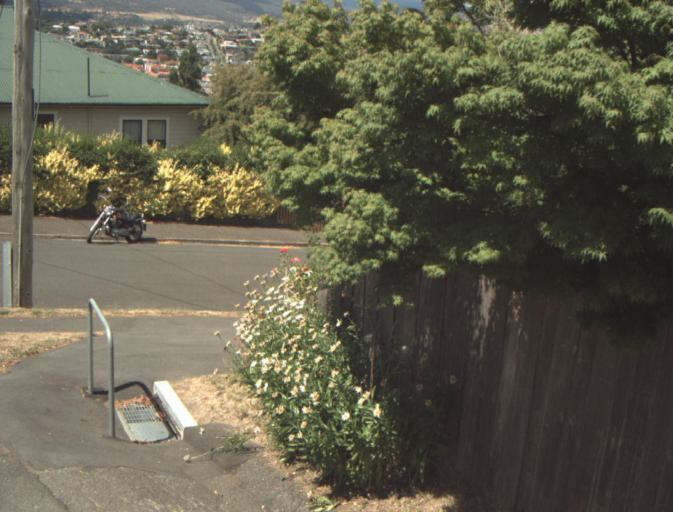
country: AU
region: Tasmania
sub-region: Launceston
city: West Launceston
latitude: -41.4468
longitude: 147.1292
